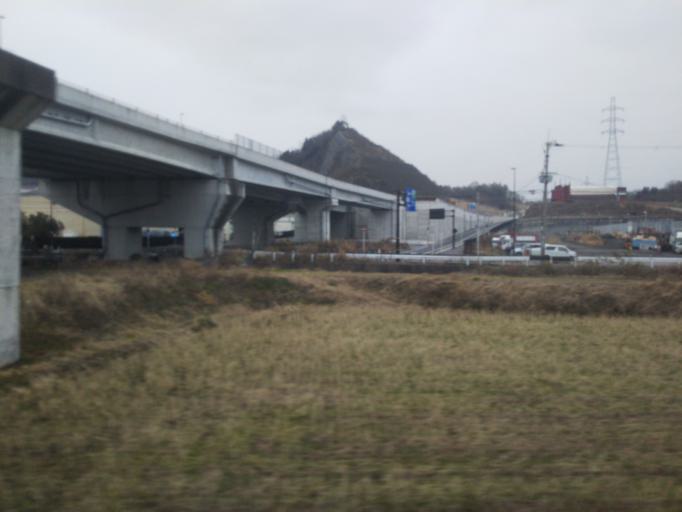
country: JP
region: Shiga Prefecture
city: Moriyama
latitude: 35.0217
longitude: 136.0462
